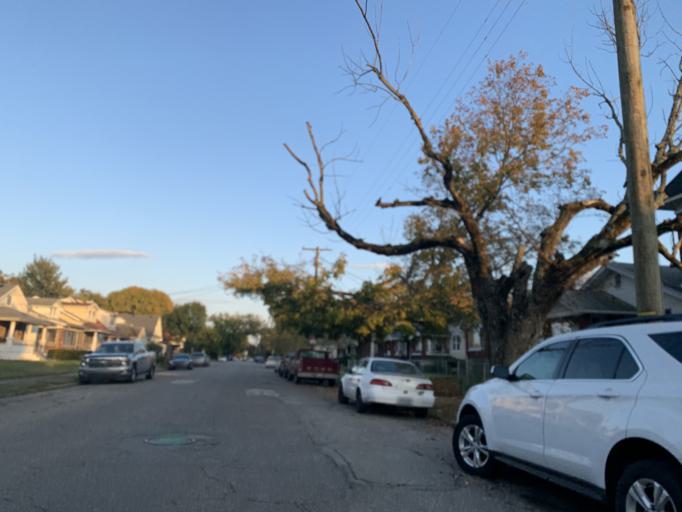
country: US
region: Indiana
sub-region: Floyd County
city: New Albany
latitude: 38.2568
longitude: -85.8180
